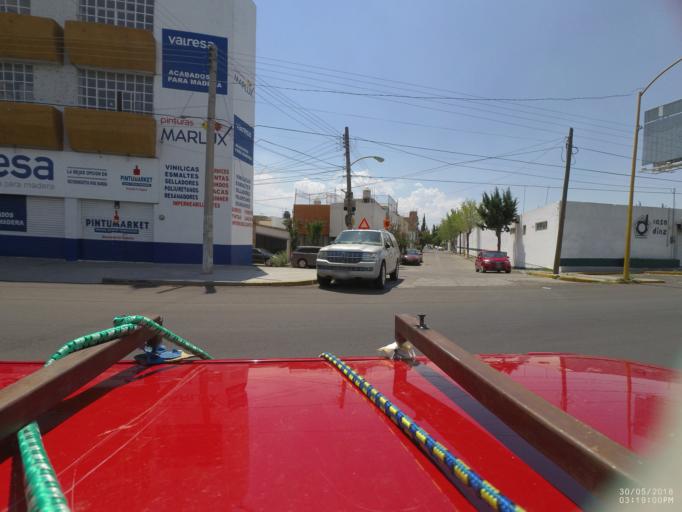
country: MX
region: Aguascalientes
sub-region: Aguascalientes
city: Aguascalientes
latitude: 21.8931
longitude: -102.3125
